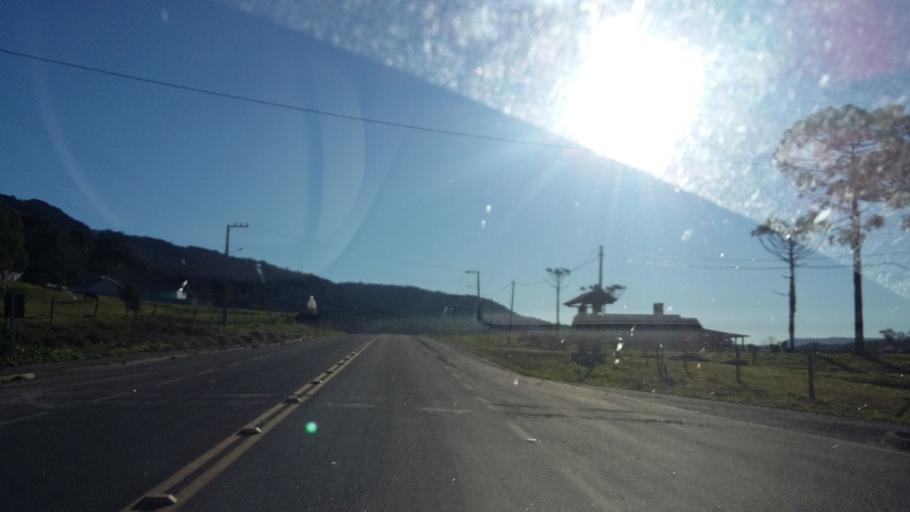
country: BR
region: Santa Catarina
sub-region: Lauro Muller
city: Lauro Muller
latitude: -28.0196
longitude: -49.5138
